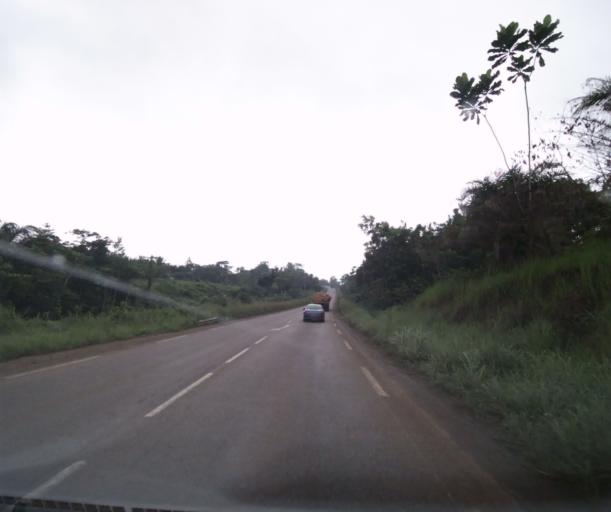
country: CM
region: Littoral
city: Edea
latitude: 3.7932
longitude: 10.2128
